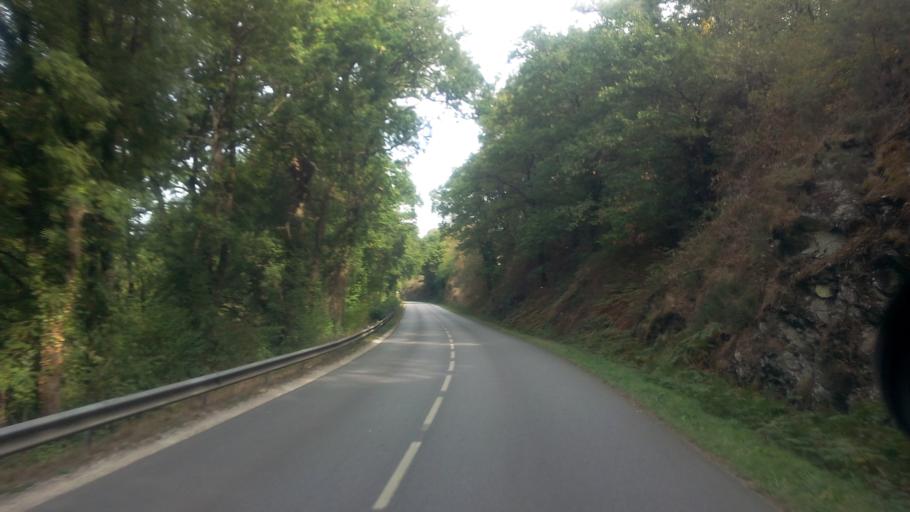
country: FR
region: Brittany
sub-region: Departement du Morbihan
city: La Gacilly
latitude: 47.7573
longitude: -2.1312
